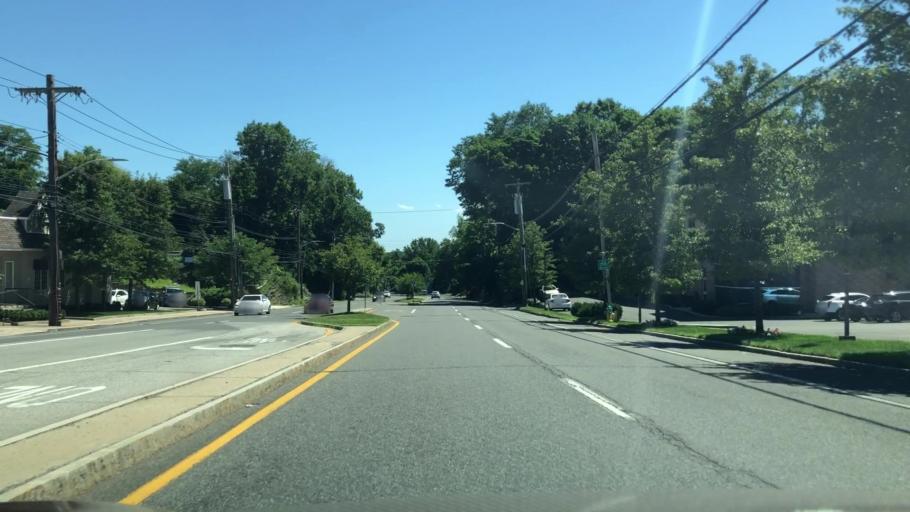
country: US
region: New York
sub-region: Westchester County
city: Scarsdale
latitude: 40.9920
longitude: -73.7462
